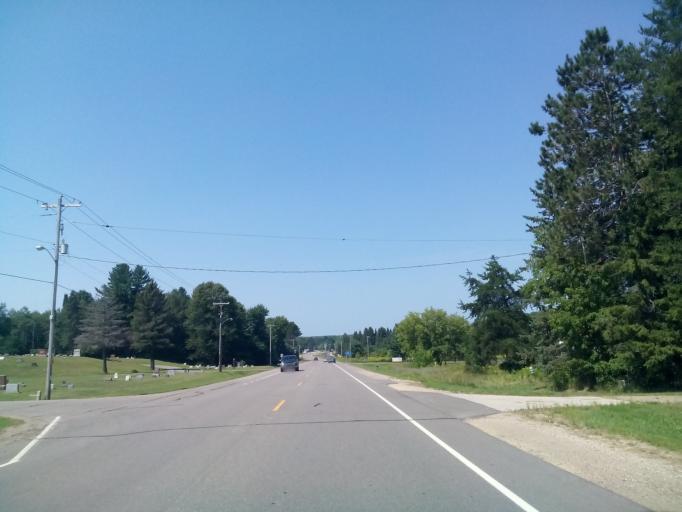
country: US
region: Wisconsin
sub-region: Menominee County
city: Legend Lake
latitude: 45.3014
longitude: -88.5321
